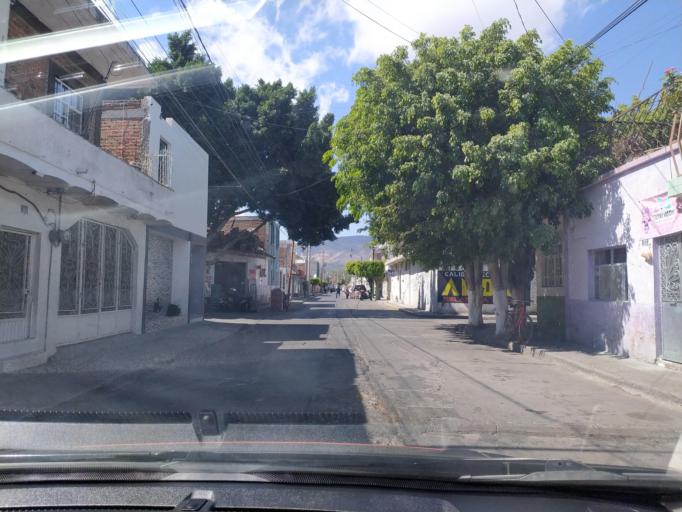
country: LA
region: Oudomxai
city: Muang La
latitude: 21.0173
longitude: 101.8640
